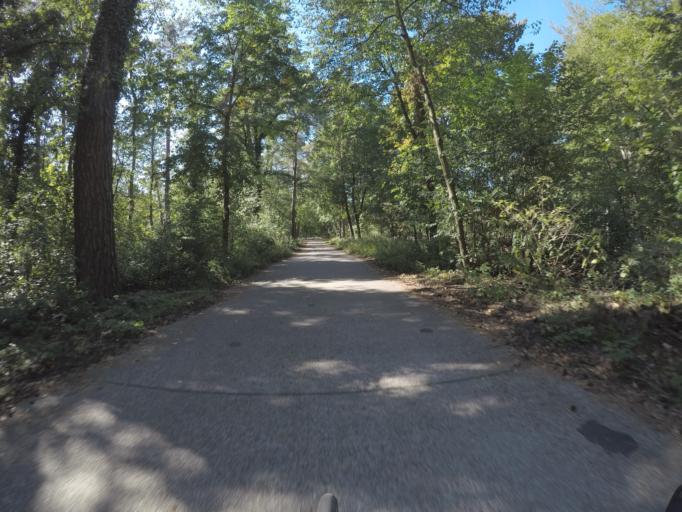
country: DE
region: Berlin
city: Konradshohe
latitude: 52.5833
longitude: 13.2501
